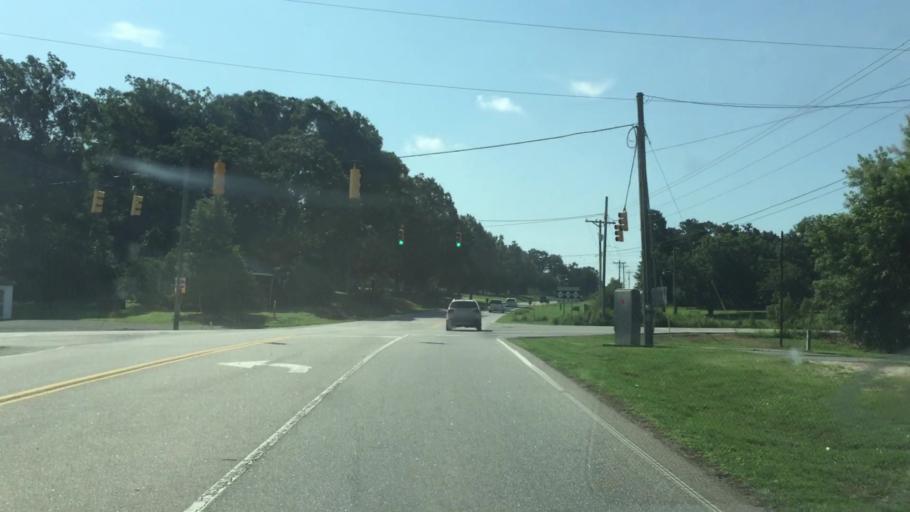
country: US
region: North Carolina
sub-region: Union County
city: Unionville
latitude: 35.1288
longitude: -80.4325
